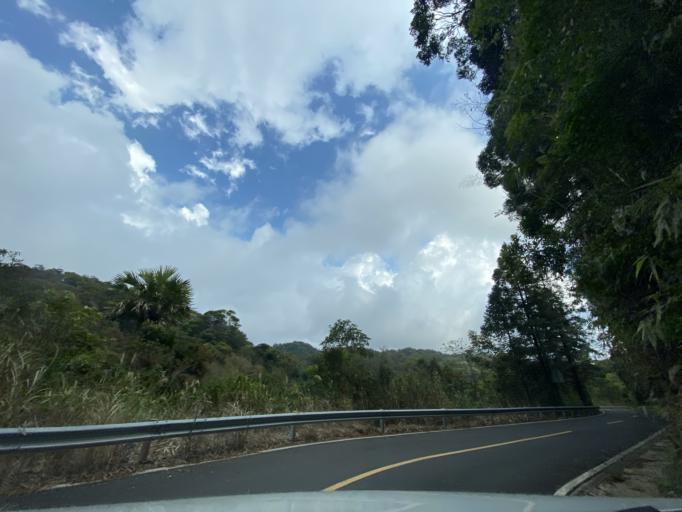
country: CN
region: Hainan
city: Diaoluoshan
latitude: 18.7197
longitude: 109.8764
